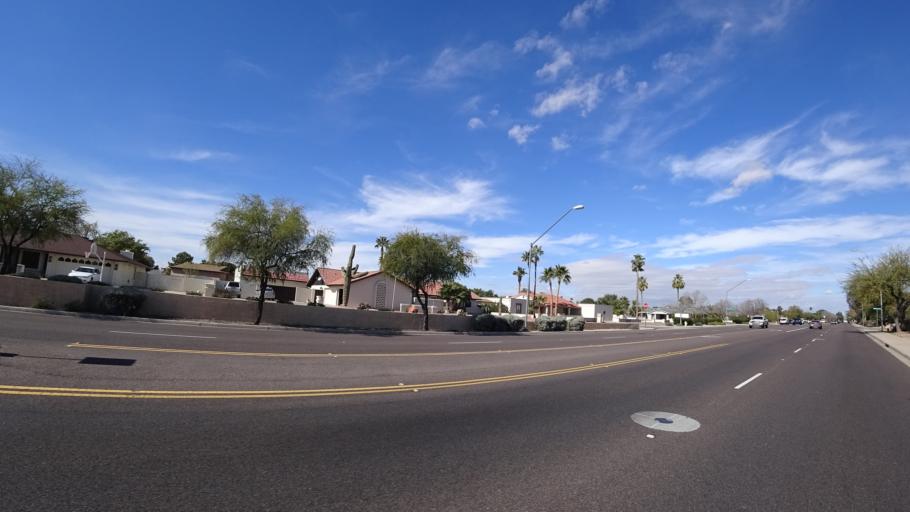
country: US
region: Arizona
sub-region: Maricopa County
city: Peoria
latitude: 33.6482
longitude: -112.2029
